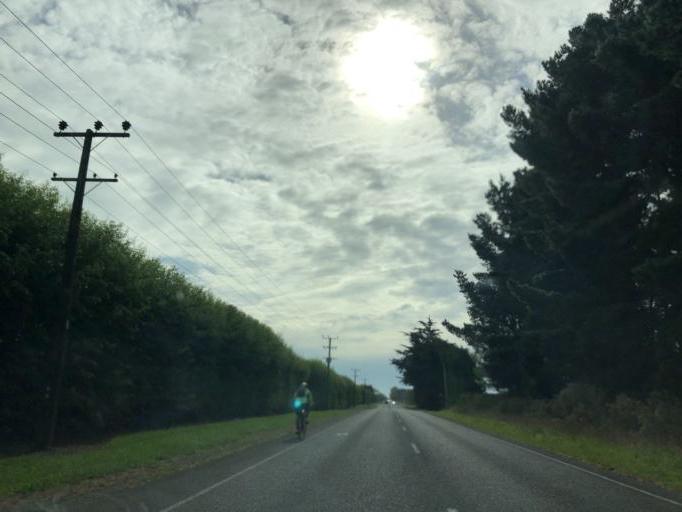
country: NZ
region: Canterbury
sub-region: Selwyn District
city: Lincoln
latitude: -43.6332
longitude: 172.4400
